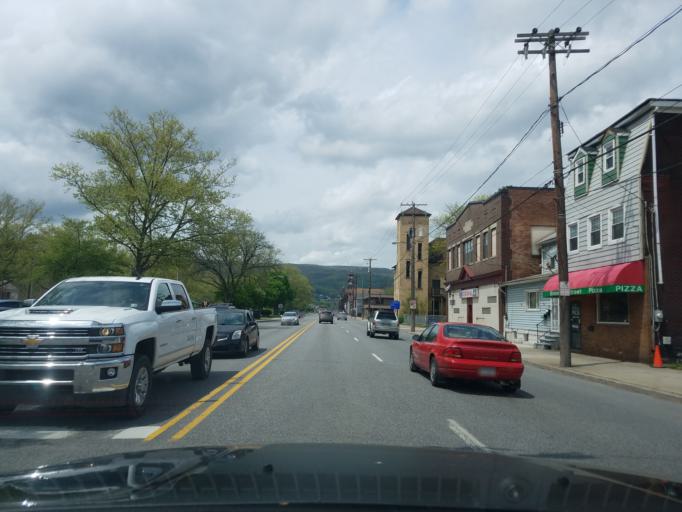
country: US
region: Pennsylvania
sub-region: Cambria County
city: Johnstown
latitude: 40.3404
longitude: -78.9302
